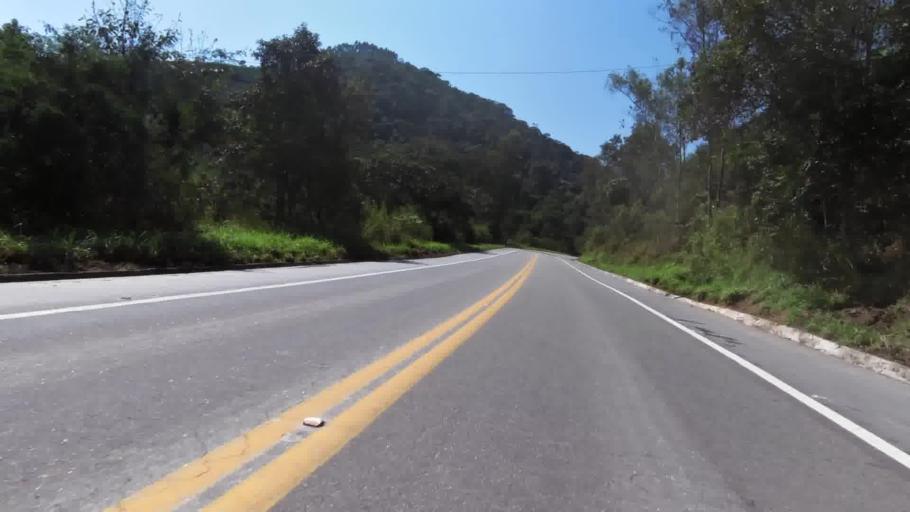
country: BR
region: Espirito Santo
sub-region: Marechal Floriano
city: Marechal Floriano
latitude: -20.4133
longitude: -40.8551
